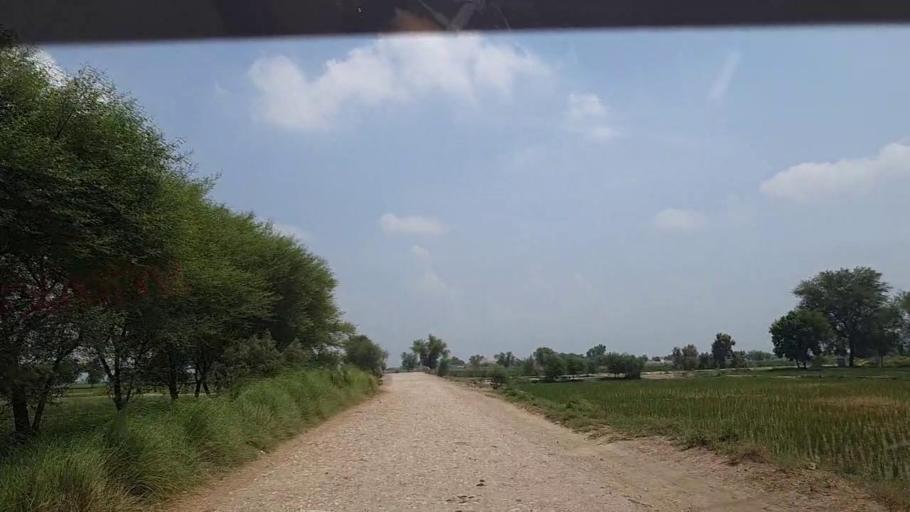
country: PK
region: Sindh
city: Khanpur
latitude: 27.8911
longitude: 69.4028
